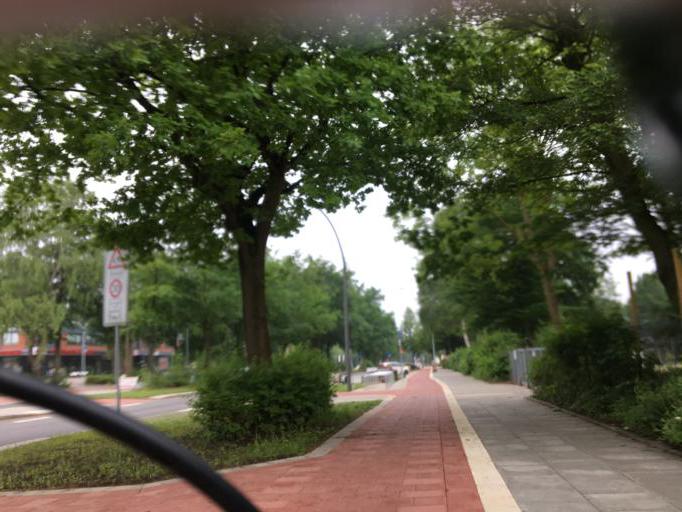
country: DE
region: Schleswig-Holstein
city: Halstenbek
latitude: 53.5828
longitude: 9.8568
